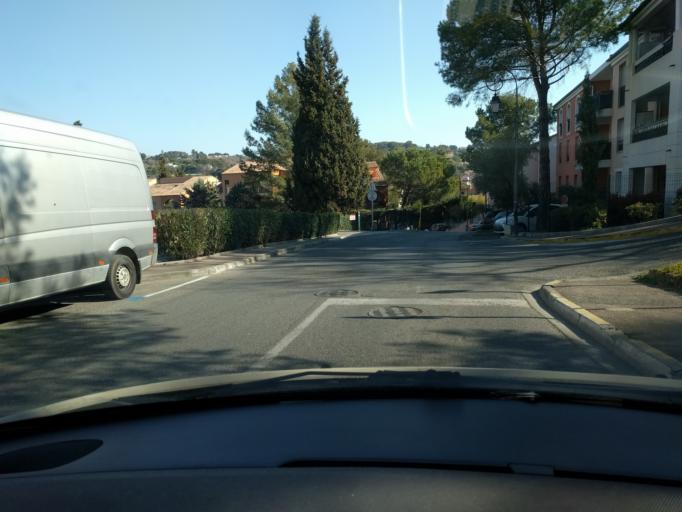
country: FR
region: Provence-Alpes-Cote d'Azur
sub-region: Departement des Alpes-Maritimes
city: Mougins
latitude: 43.6010
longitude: 6.9873
